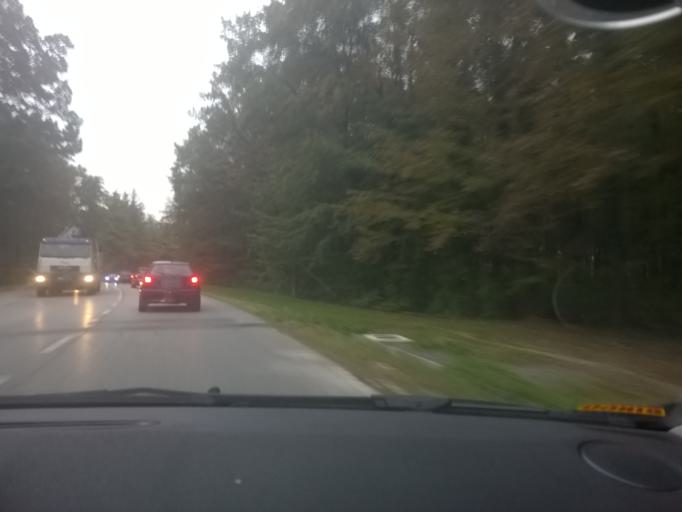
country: HR
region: Zagrebacka
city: Brdovec
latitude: 45.8792
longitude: 15.8000
